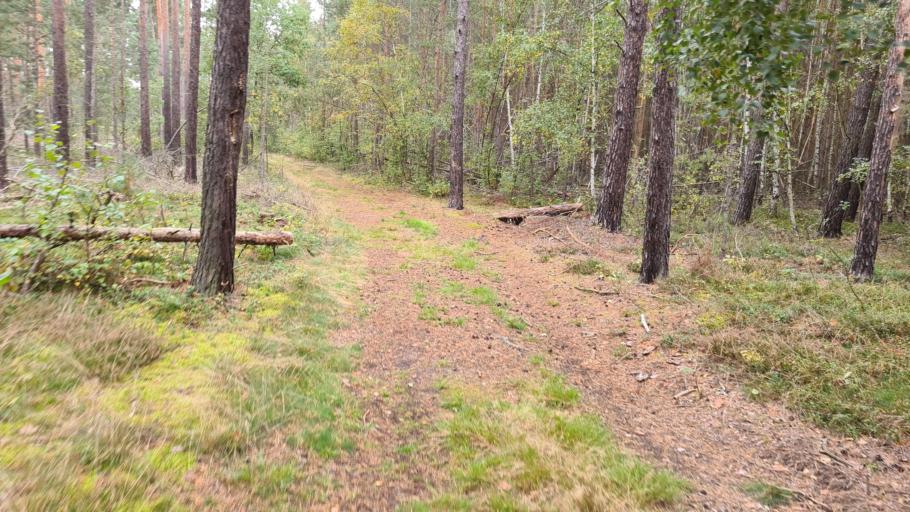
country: DE
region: Brandenburg
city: Schonewalde
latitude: 51.6319
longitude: 13.6118
